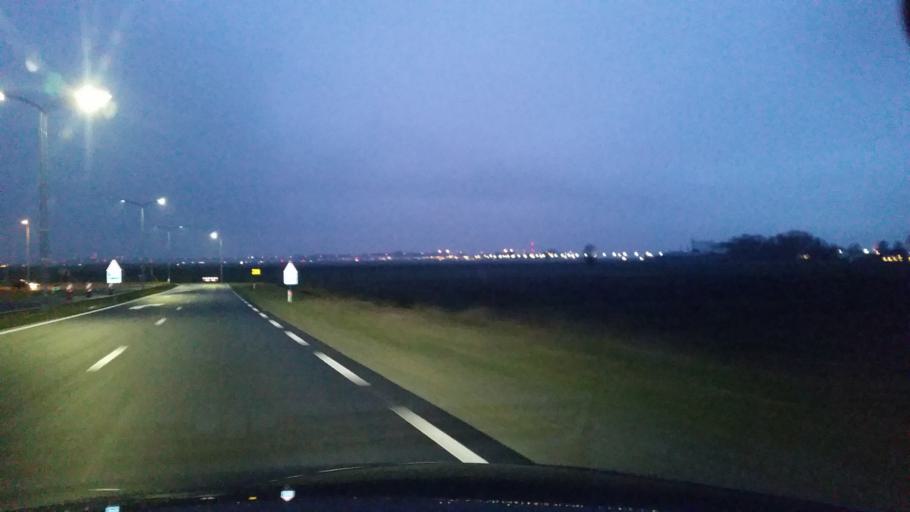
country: NL
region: North Holland
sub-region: Gemeente Haarlemmermeer
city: Hoofddorp
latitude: 52.3419
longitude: 4.7543
